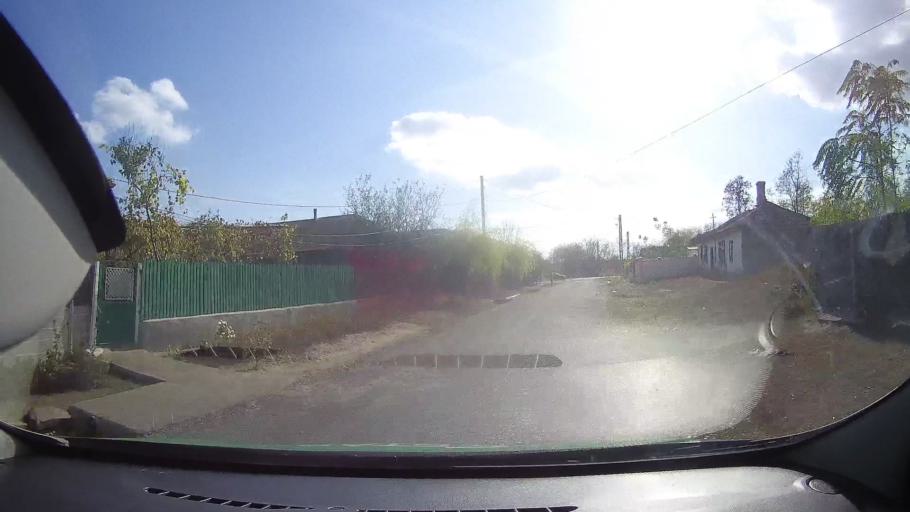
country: RO
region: Constanta
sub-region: Comuna Istria
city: Istria
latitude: 44.5727
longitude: 28.7147
